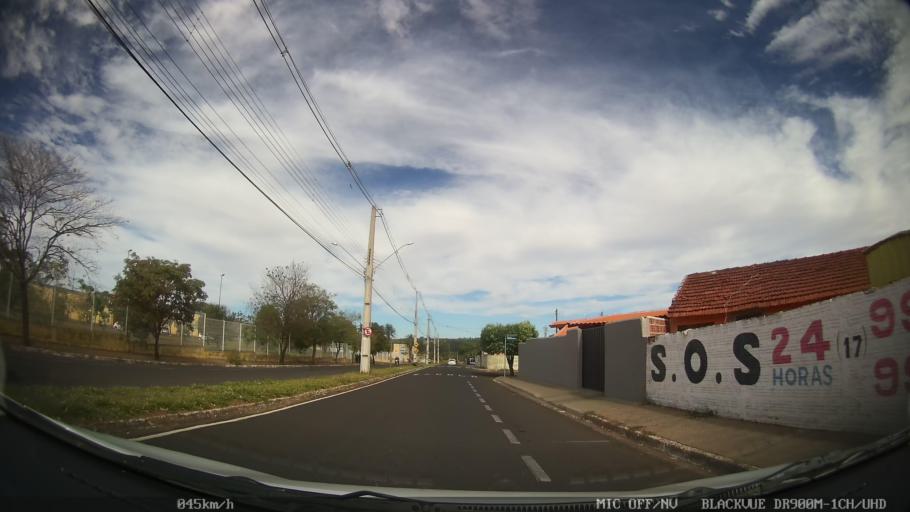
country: BR
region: Sao Paulo
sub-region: Catanduva
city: Catanduva
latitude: -21.1461
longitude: -48.9468
